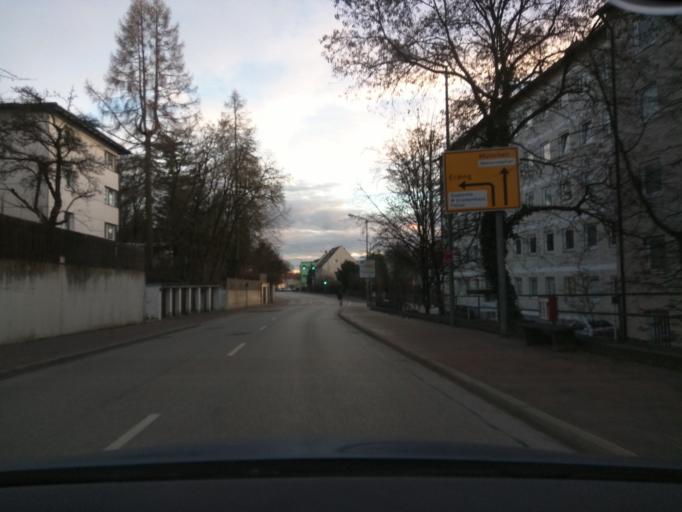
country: DE
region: Bavaria
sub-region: Upper Bavaria
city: Freising
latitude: 48.4012
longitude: 11.7370
